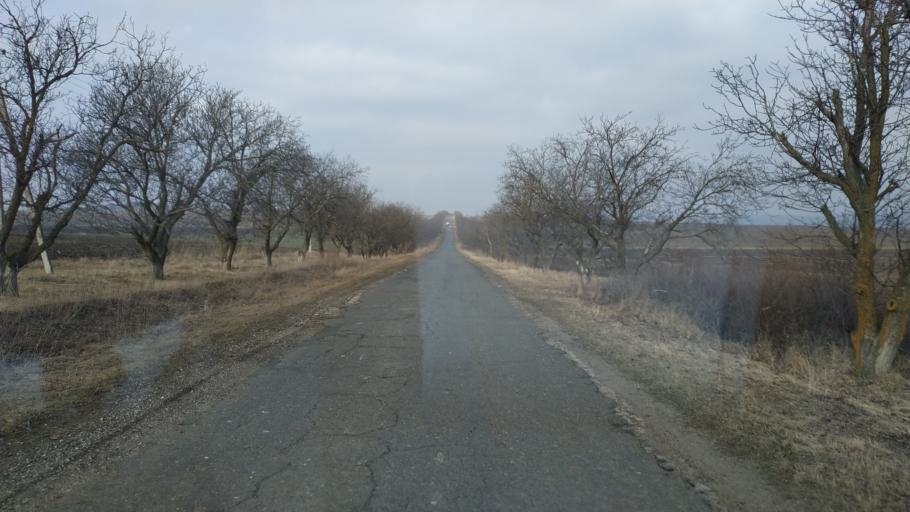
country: MD
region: Hincesti
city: Dancu
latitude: 46.8704
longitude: 28.2943
